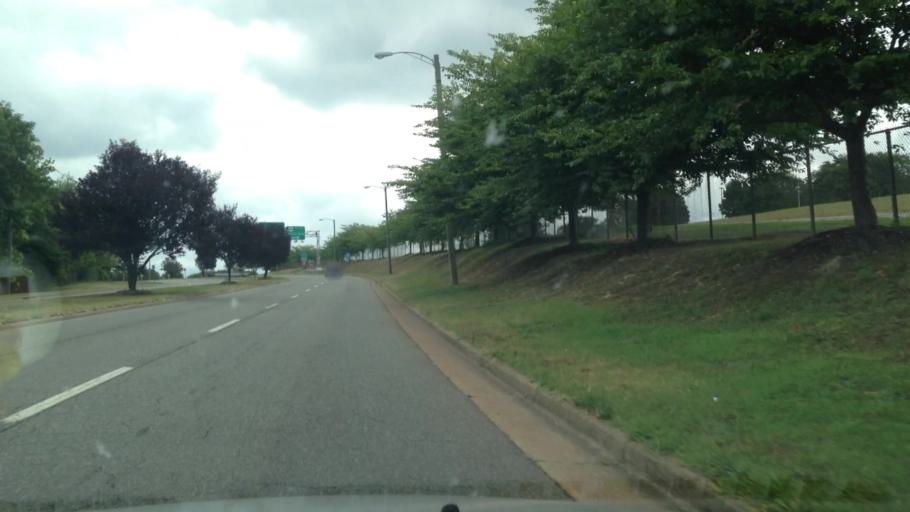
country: US
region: Virginia
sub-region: City of Danville
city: Danville
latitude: 36.5873
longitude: -79.4145
